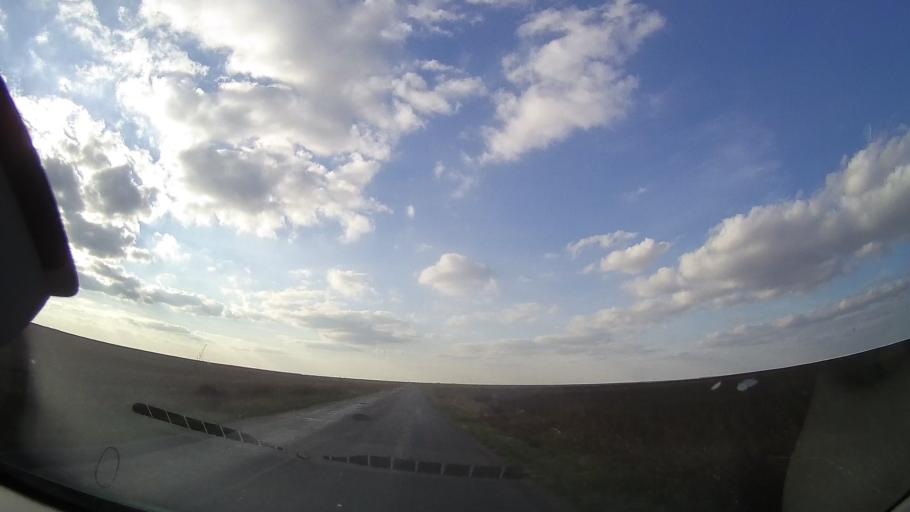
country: RO
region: Constanta
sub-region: Comuna Negru Voda
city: Negru Voda
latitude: 43.8207
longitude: 28.1699
